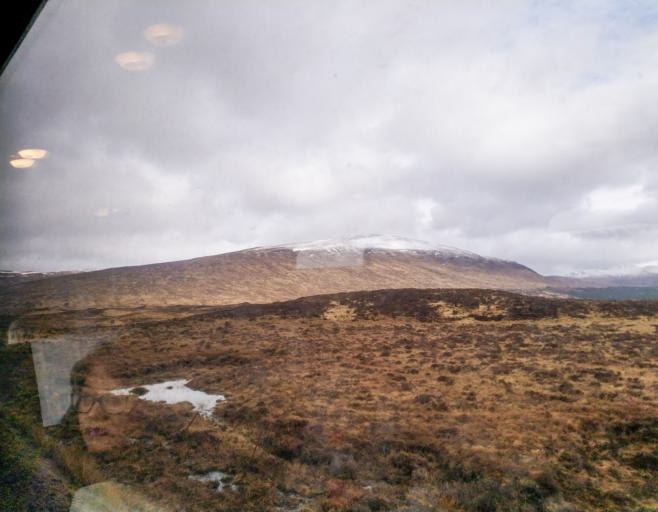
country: GB
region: Scotland
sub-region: Highland
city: Spean Bridge
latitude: 56.7551
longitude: -4.6850
